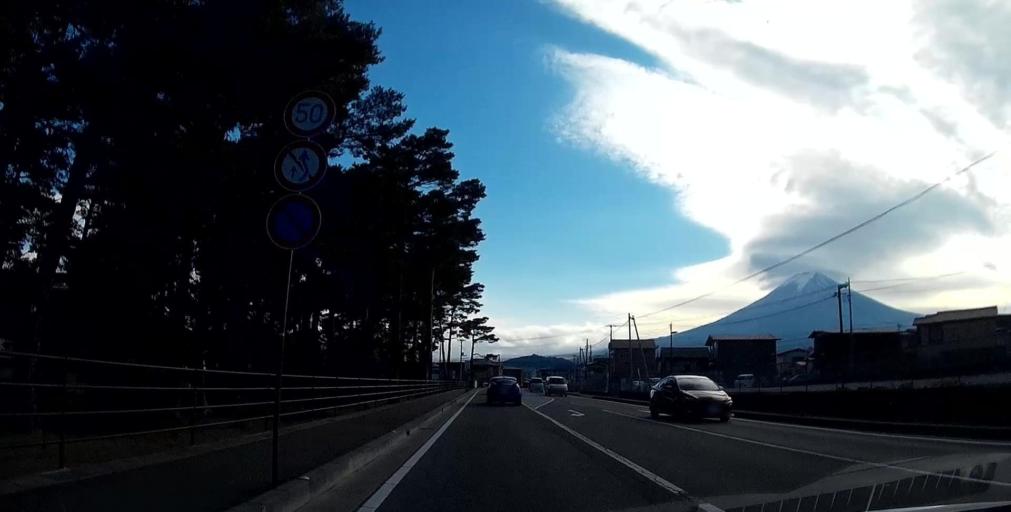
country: JP
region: Yamanashi
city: Fujikawaguchiko
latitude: 35.4940
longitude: 138.7932
